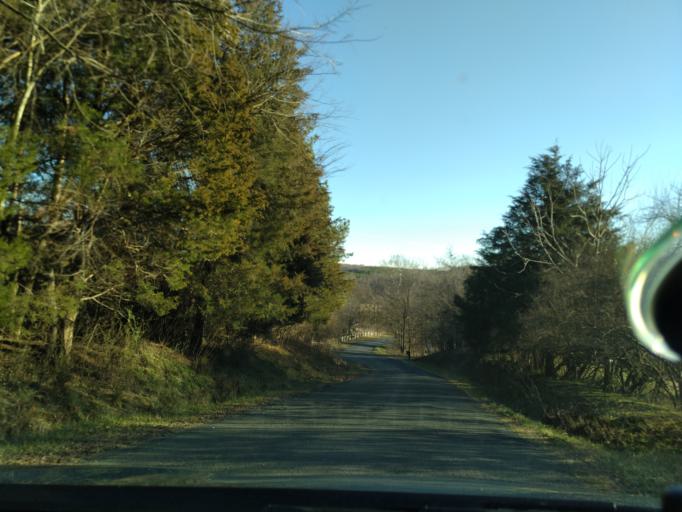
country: US
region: Virginia
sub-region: Appomattox County
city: Appomattox
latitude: 37.3758
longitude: -78.6402
